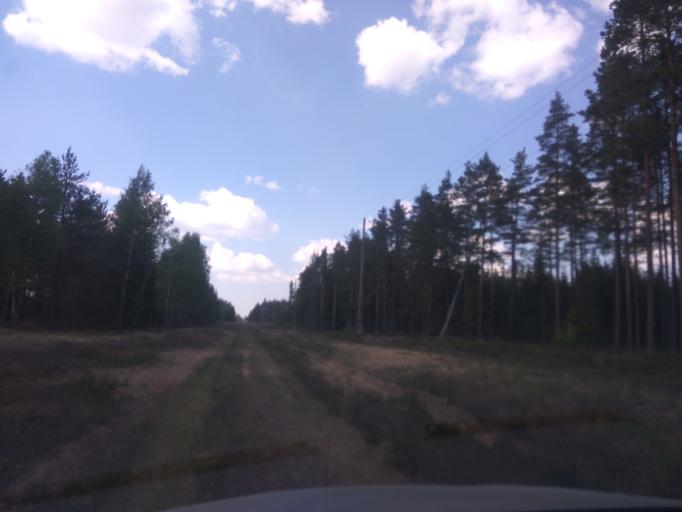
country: LV
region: Kuldigas Rajons
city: Kuldiga
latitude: 57.1830
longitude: 21.9979
